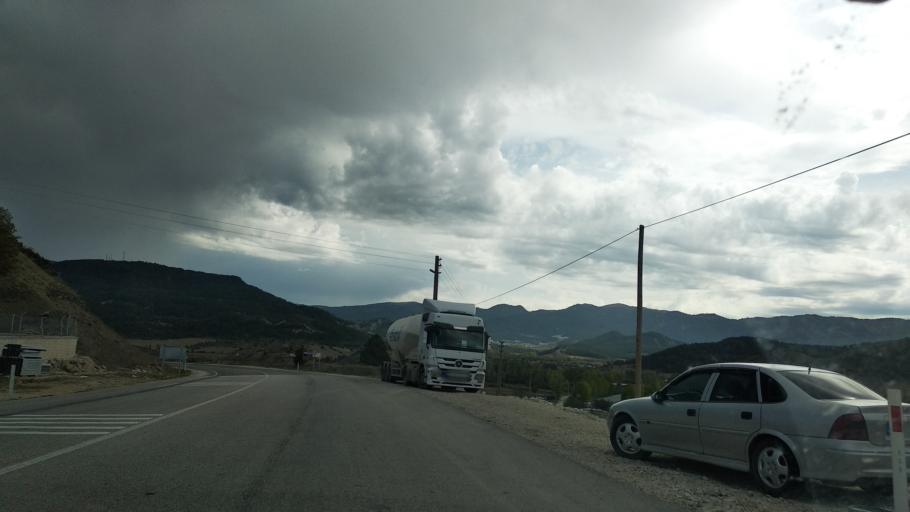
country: TR
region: Bolu
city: Mudurnu
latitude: 40.4788
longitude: 31.1595
